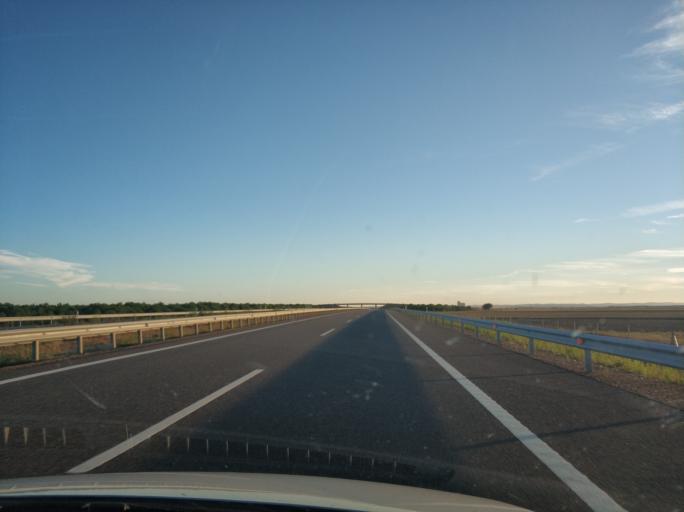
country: ES
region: Castille and Leon
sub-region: Provincia de Zamora
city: Barcial del Barco
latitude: 41.9512
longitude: -5.6239
